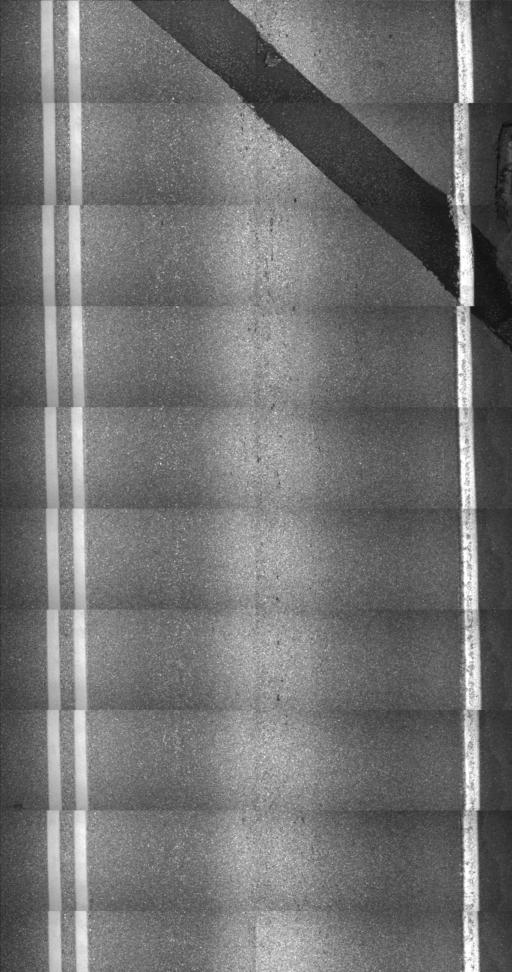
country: US
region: Vermont
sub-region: Windham County
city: Dover
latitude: 42.9363
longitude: -72.8488
